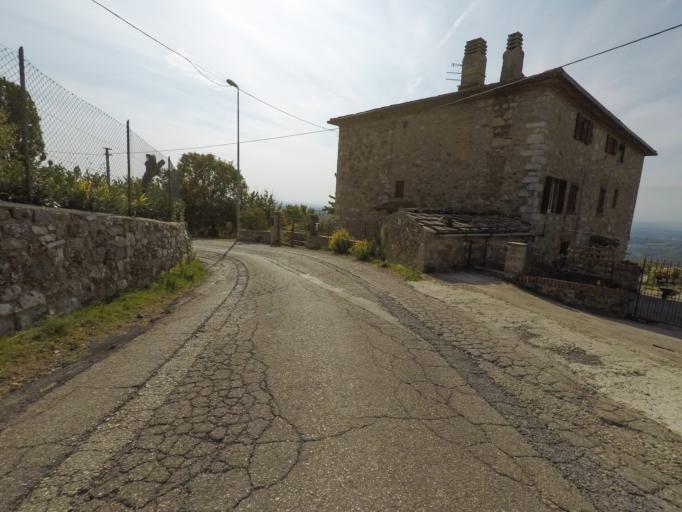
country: IT
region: Tuscany
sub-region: Provincia di Siena
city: Castellina in Chianti
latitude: 43.4202
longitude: 11.3400
